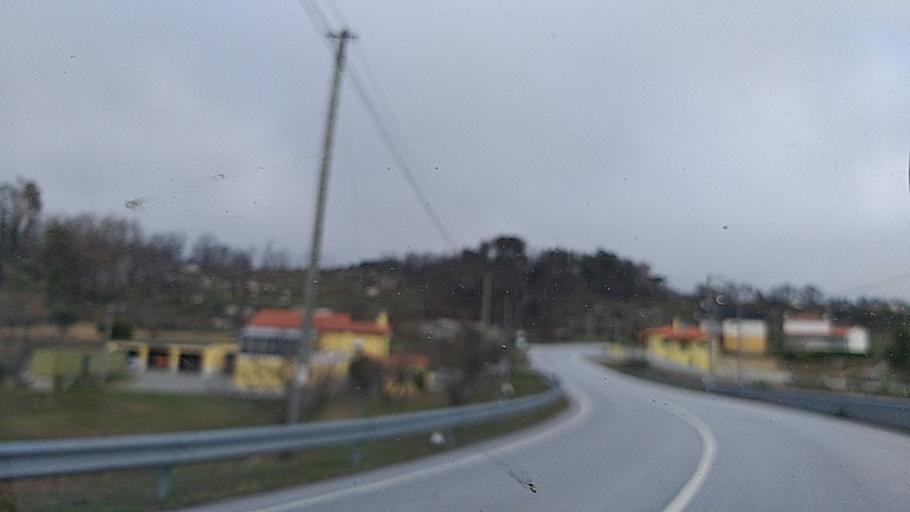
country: PT
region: Guarda
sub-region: Fornos de Algodres
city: Fornos de Algodres
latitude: 40.6767
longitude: -7.4718
